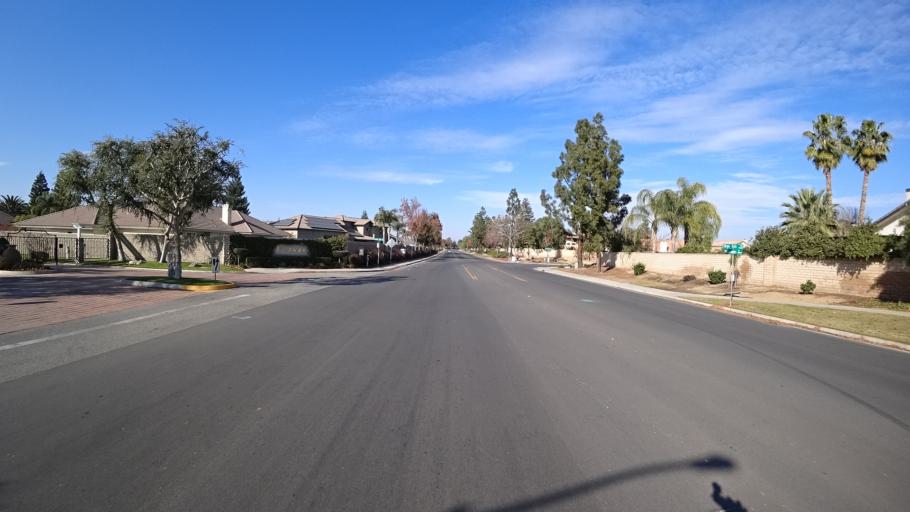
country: US
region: California
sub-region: Kern County
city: Greenacres
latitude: 35.4015
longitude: -119.0980
